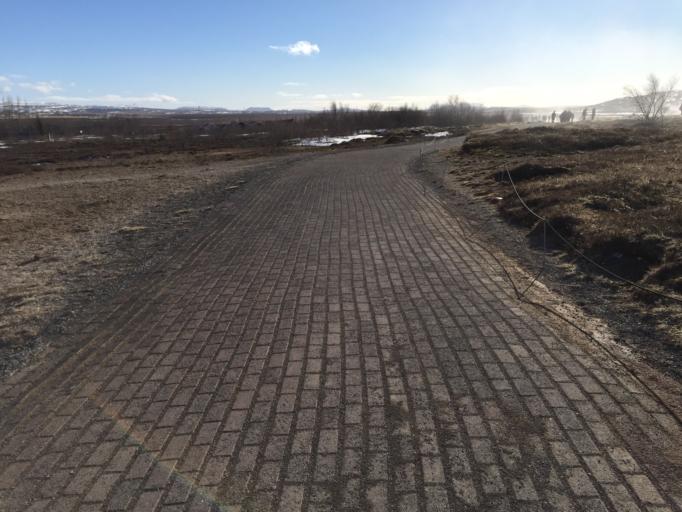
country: IS
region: South
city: Selfoss
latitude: 64.3132
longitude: -20.2992
